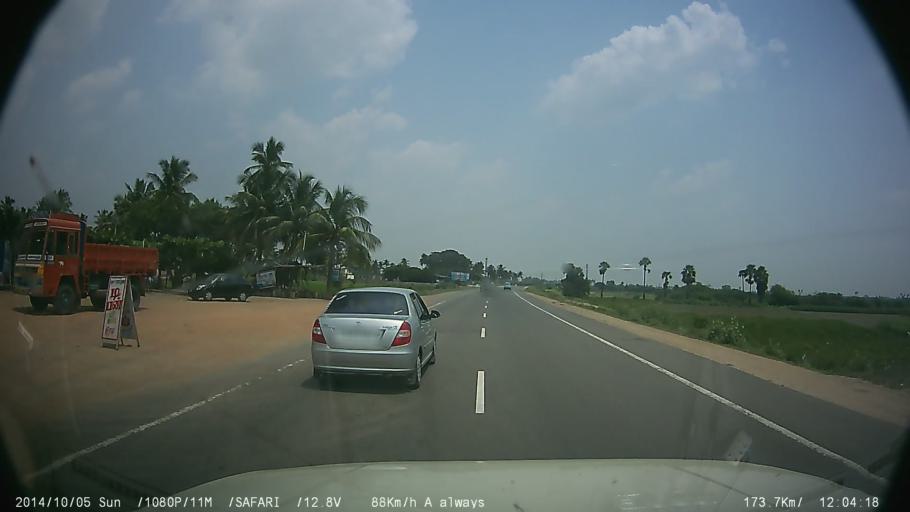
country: IN
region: Tamil Nadu
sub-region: Villupuram
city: Chinna Salem
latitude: 11.6437
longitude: 78.8744
